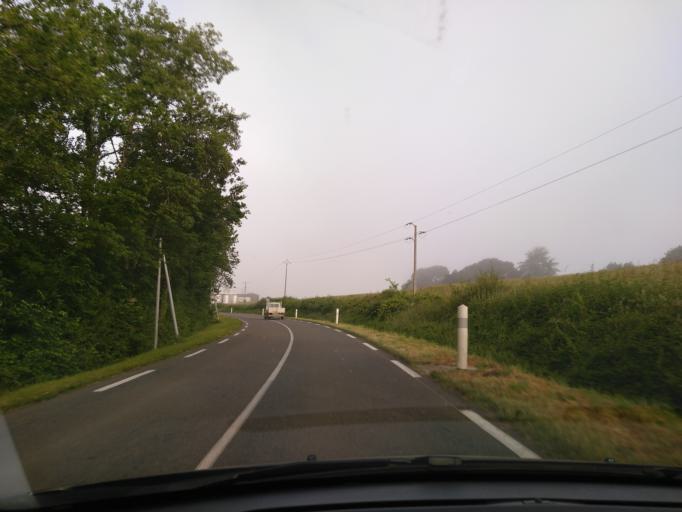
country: FR
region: Midi-Pyrenees
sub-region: Departement du Gers
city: Gondrin
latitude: 43.8782
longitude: 0.1741
